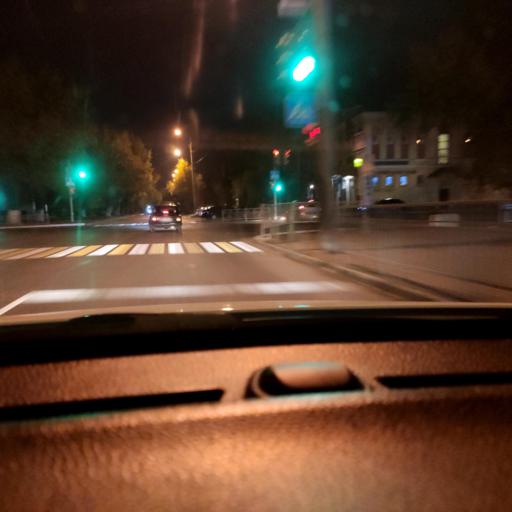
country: RU
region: Voronezj
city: Voronezh
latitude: 51.6424
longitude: 39.2411
